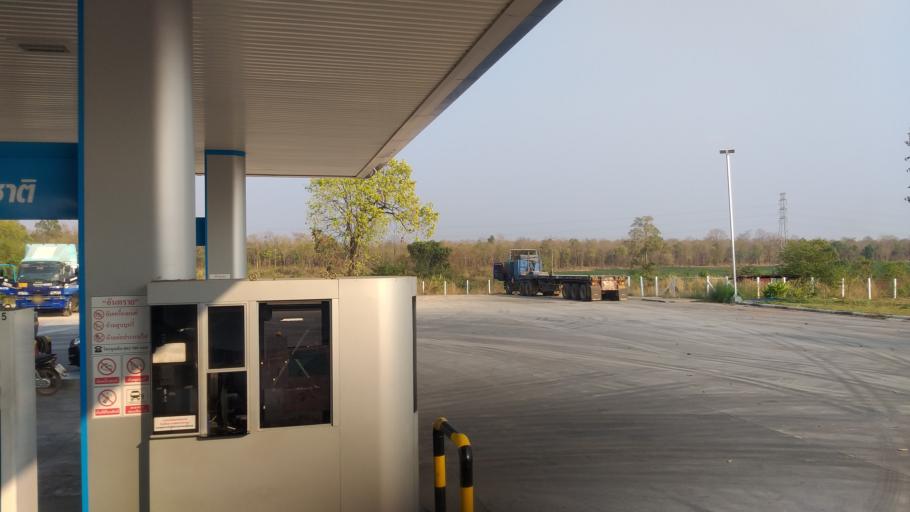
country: TH
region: Khon Kaen
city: Nam Phong
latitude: 16.6848
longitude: 102.8057
